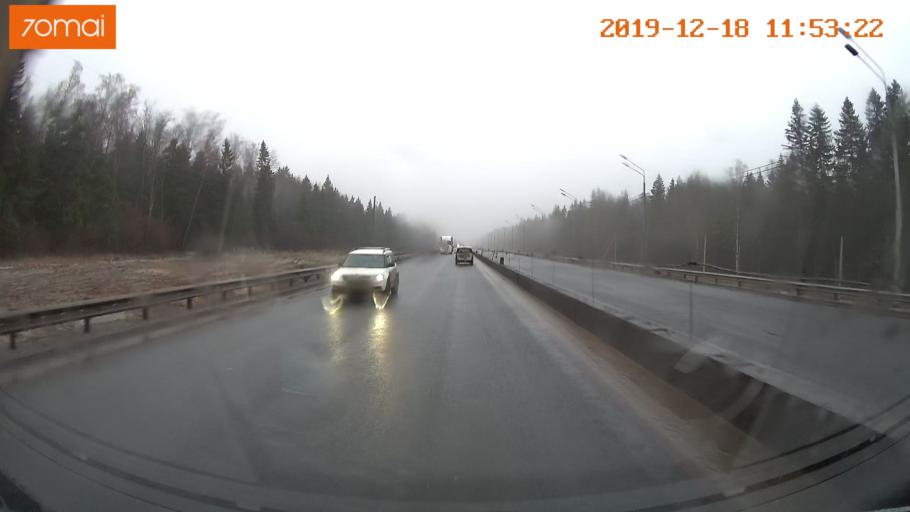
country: RU
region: Moskovskaya
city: Yershovo
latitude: 55.8033
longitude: 36.9201
